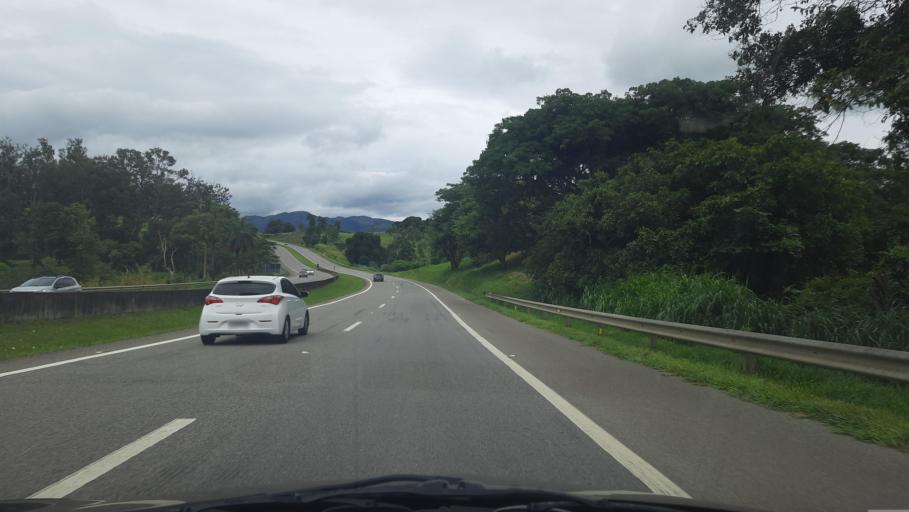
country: BR
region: Sao Paulo
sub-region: Sao Joao Da Boa Vista
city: Sao Joao da Boa Vista
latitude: -21.9709
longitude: -46.7429
